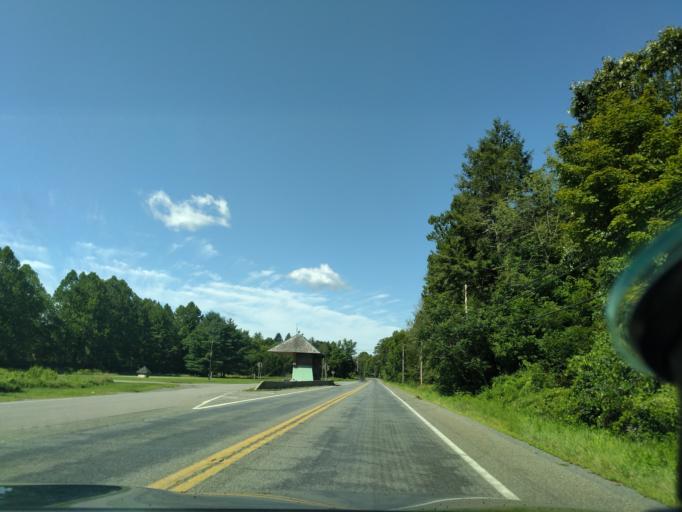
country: US
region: Pennsylvania
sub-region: Pike County
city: Saw Creek
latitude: 41.0828
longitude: -75.0150
